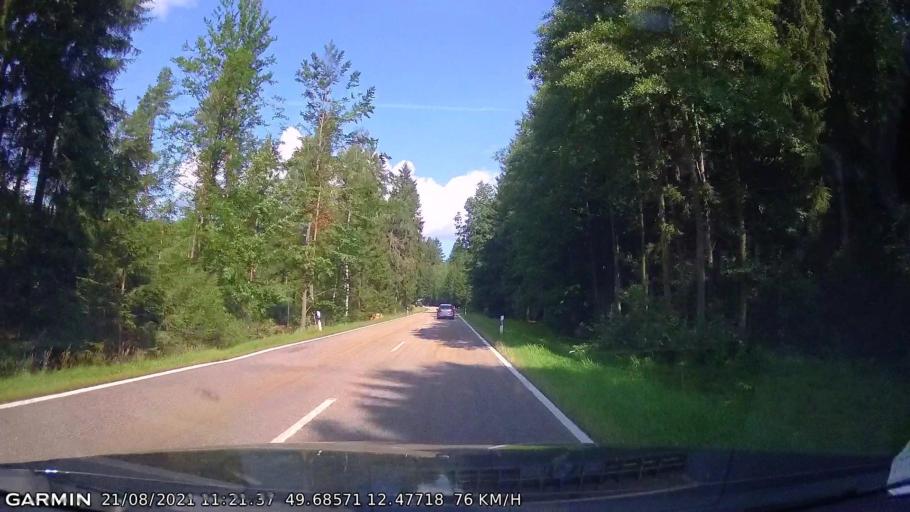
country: DE
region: Bavaria
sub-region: Upper Palatinate
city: Waidhaus
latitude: 49.6857
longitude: 12.4772
